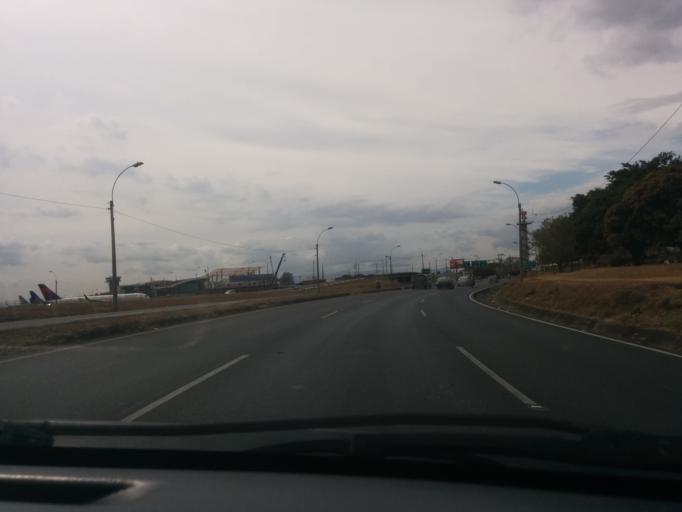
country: CR
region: Alajuela
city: Alajuela
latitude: 9.9992
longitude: -84.1988
